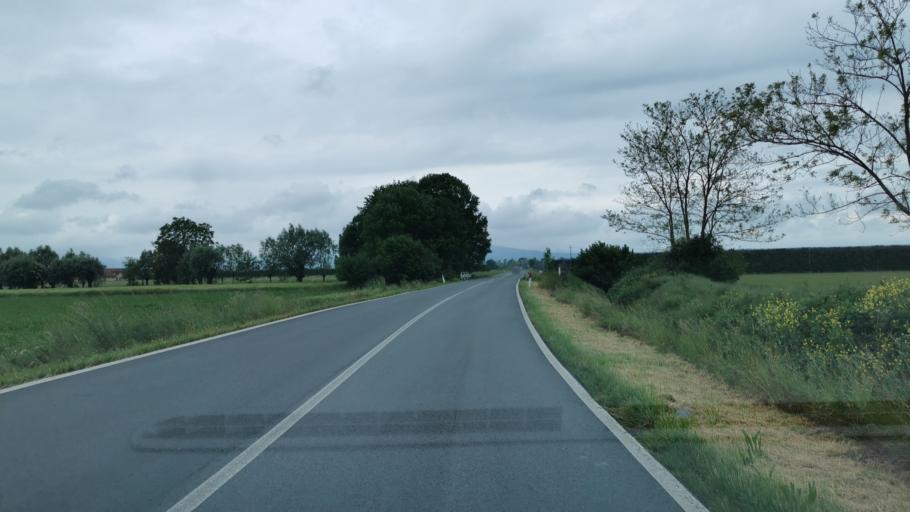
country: IT
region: Piedmont
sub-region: Provincia di Cuneo
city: Lagnasco
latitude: 44.6038
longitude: 7.5781
